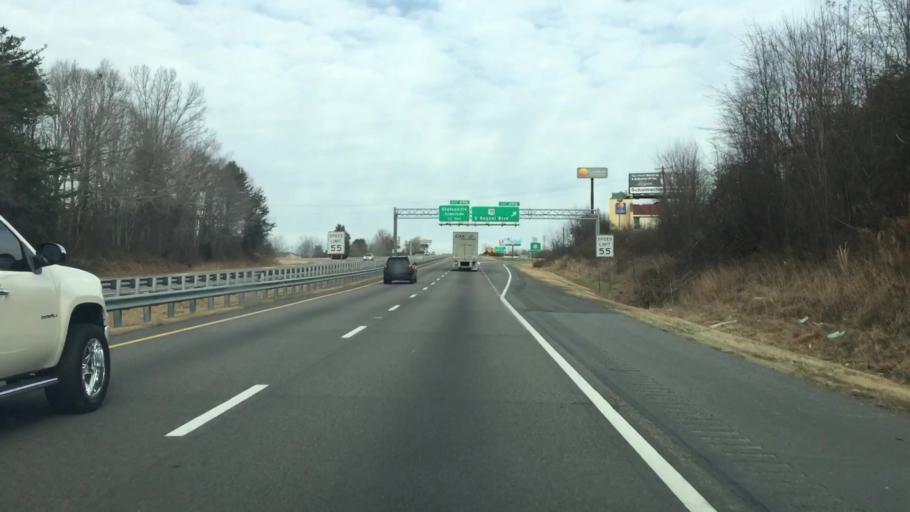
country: US
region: North Carolina
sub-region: Iredell County
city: Statesville
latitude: 35.7678
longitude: -80.8625
